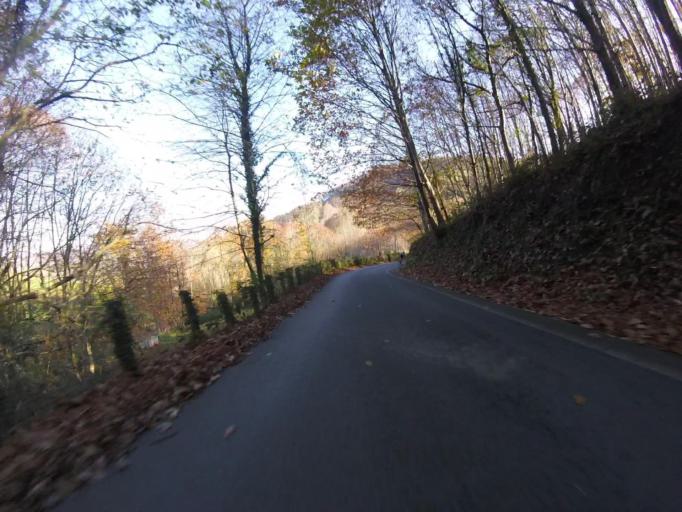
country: ES
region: Navarre
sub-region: Provincia de Navarra
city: Igantzi
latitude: 43.2317
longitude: -1.7028
